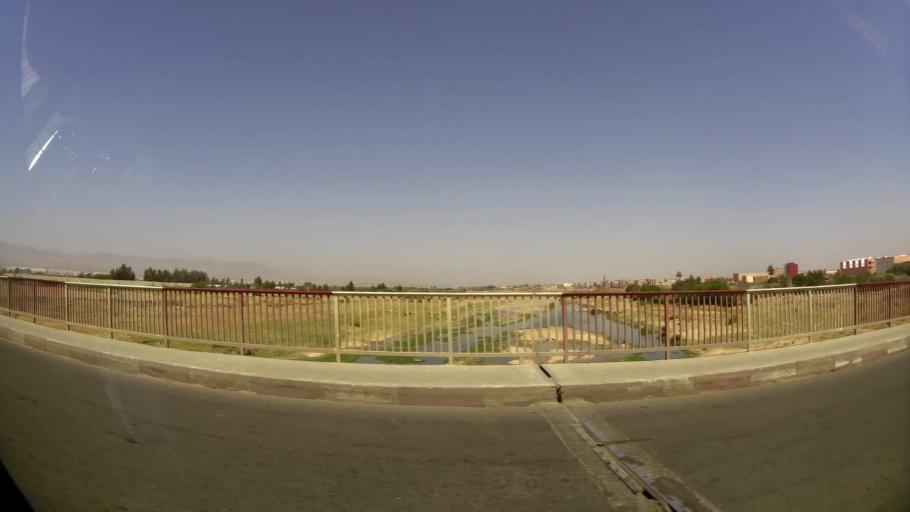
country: MA
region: Souss-Massa-Draa
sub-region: Inezgane-Ait Mellou
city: Inezgane
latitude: 30.3515
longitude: -9.5049
